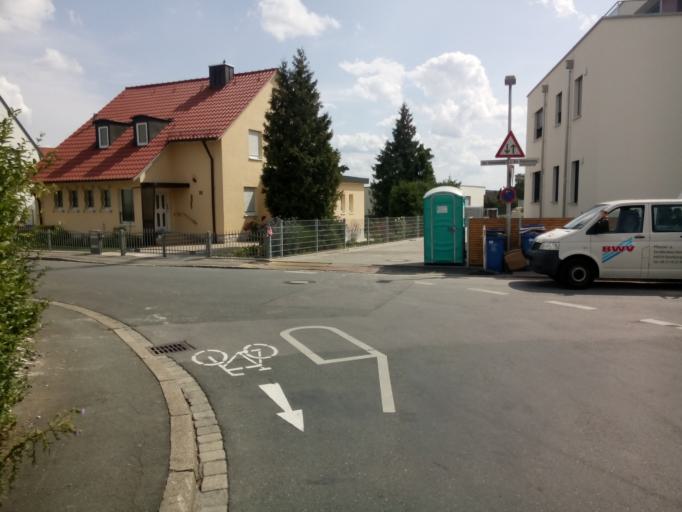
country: DE
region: Bavaria
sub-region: Upper Franconia
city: Bamberg
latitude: 49.8773
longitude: 10.8797
